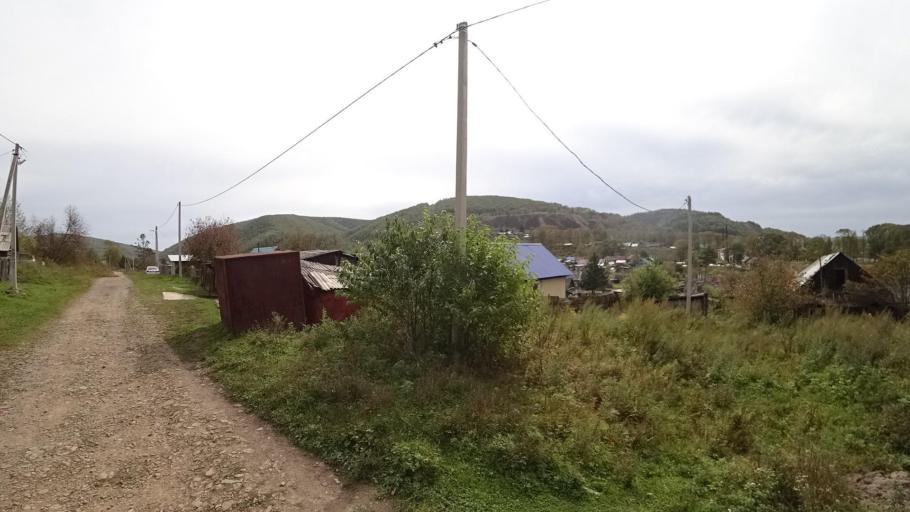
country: RU
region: Jewish Autonomous Oblast
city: Khingansk
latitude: 49.1292
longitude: 131.2000
